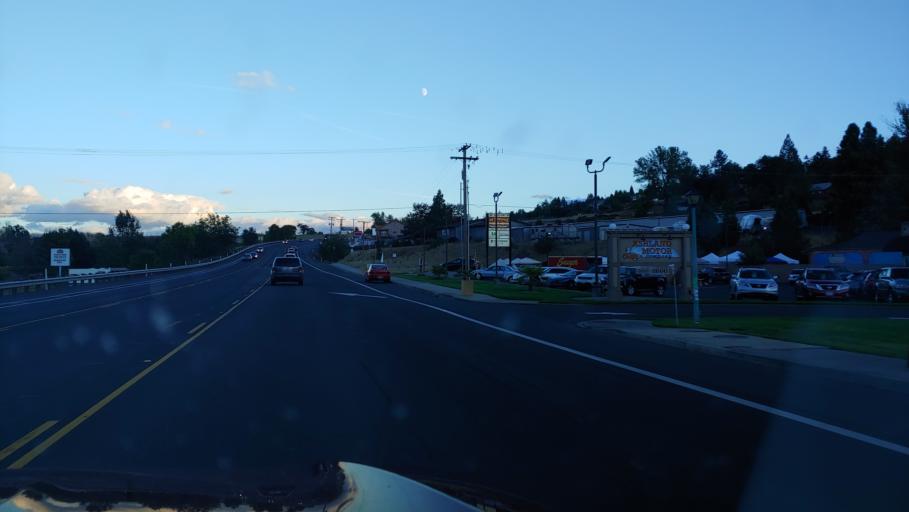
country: US
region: Oregon
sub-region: Jackson County
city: Ashland
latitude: 42.2187
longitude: -122.7369
